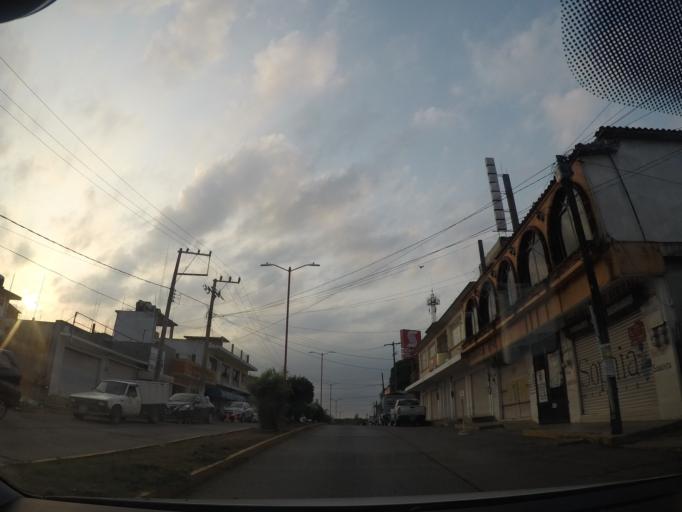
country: MX
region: Oaxaca
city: Matias Romero
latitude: 16.8772
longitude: -95.0416
